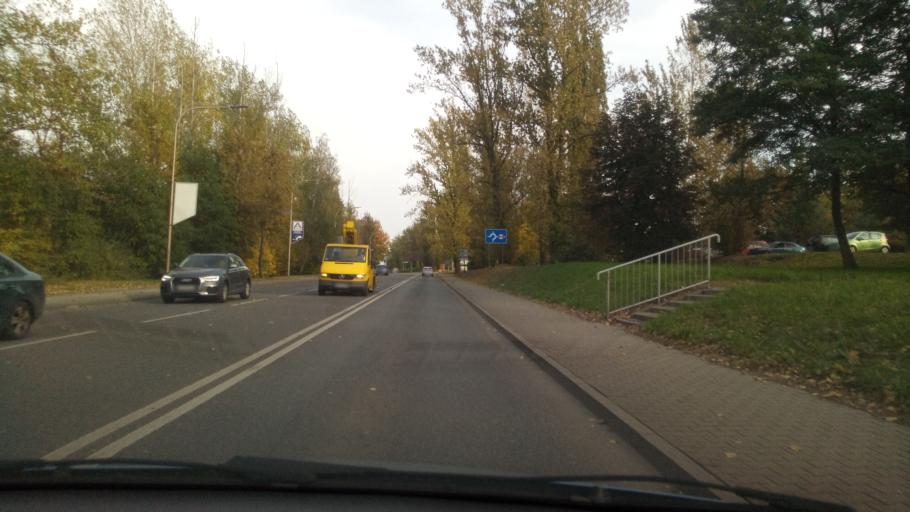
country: PL
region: Silesian Voivodeship
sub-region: Sosnowiec
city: Sosnowiec
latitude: 50.2482
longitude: 19.1210
